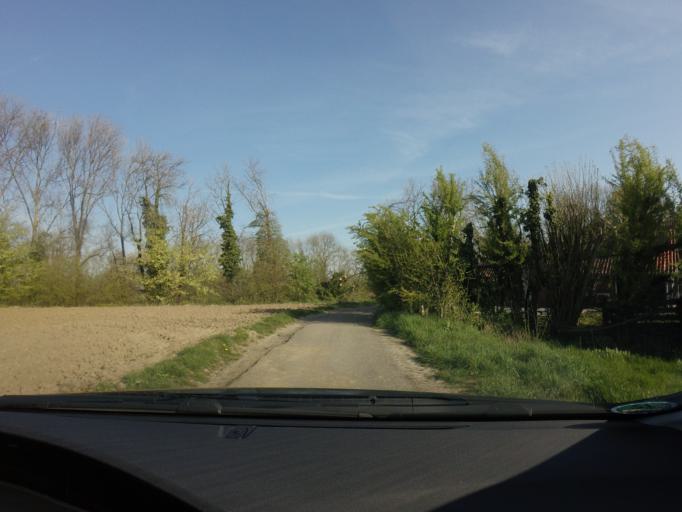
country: NL
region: Limburg
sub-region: Gemeente Stein
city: Elsloo
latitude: 50.9408
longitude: 5.7573
